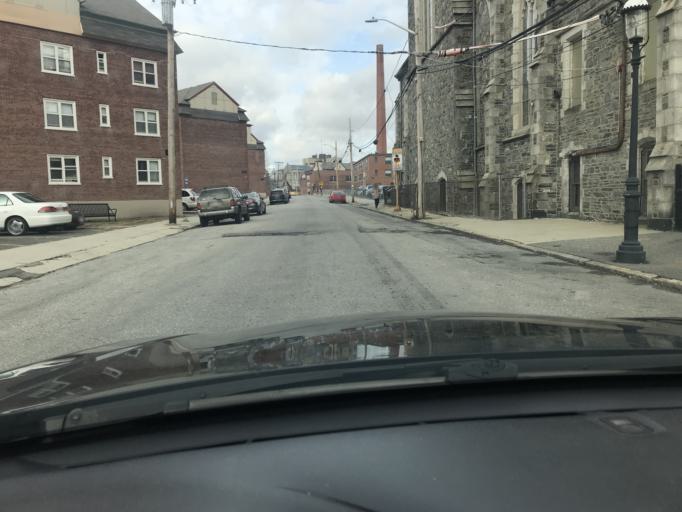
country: US
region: Massachusetts
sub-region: Middlesex County
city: Lowell
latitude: 42.6450
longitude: -71.3189
